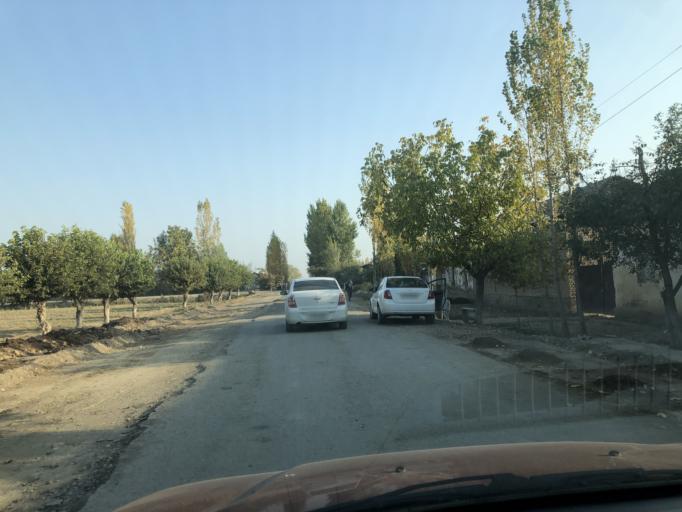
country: UZ
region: Namangan
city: Uychi
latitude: 41.0648
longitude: 71.9870
